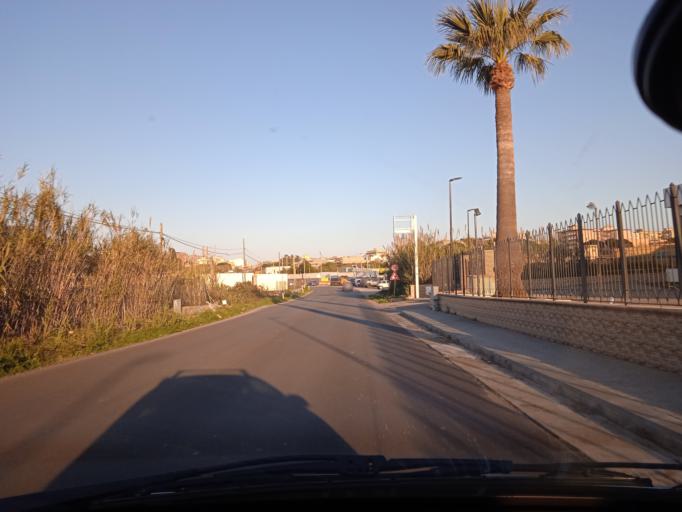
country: IT
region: Sicily
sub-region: Palermo
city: Bagheria
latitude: 38.0888
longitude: 13.4946
